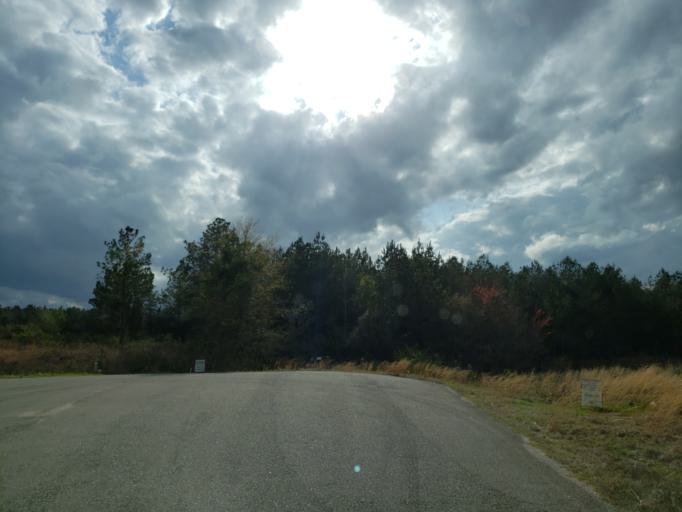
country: US
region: Mississippi
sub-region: Jones County
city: Ellisville
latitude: 31.5527
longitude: -89.2596
